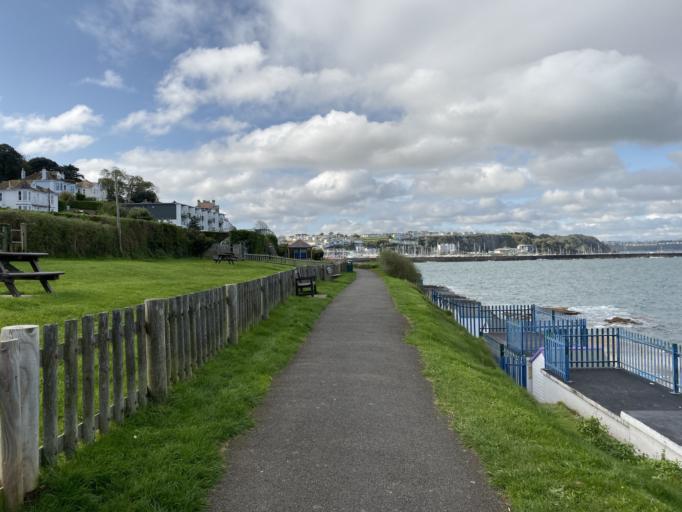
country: GB
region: England
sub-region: Borough of Torbay
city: Brixham
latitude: 50.4011
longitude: -3.4991
